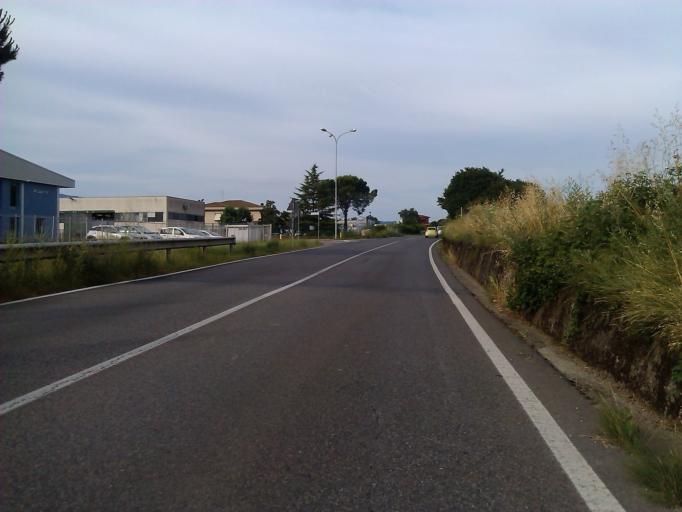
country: IT
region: Tuscany
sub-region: Province of Arezzo
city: Bucine
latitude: 43.4938
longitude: 11.6330
